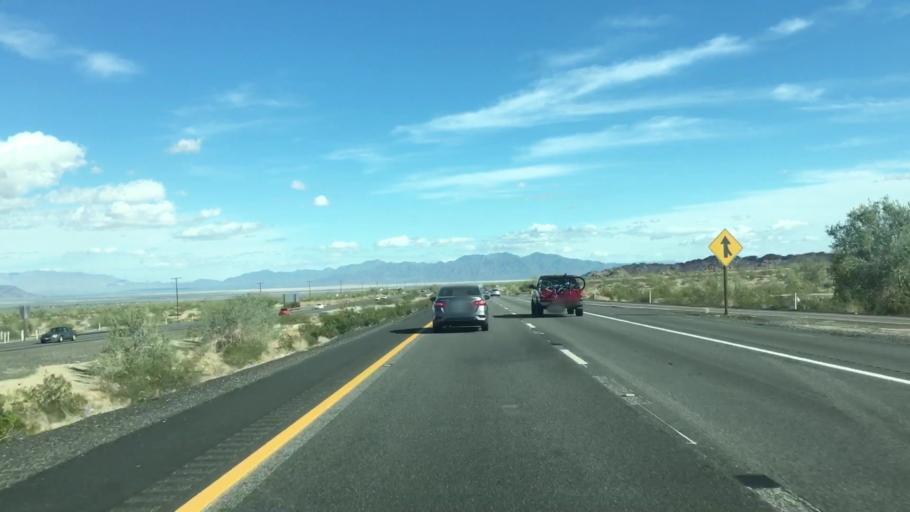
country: US
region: California
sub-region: Imperial County
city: Niland
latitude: 33.7022
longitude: -115.4510
